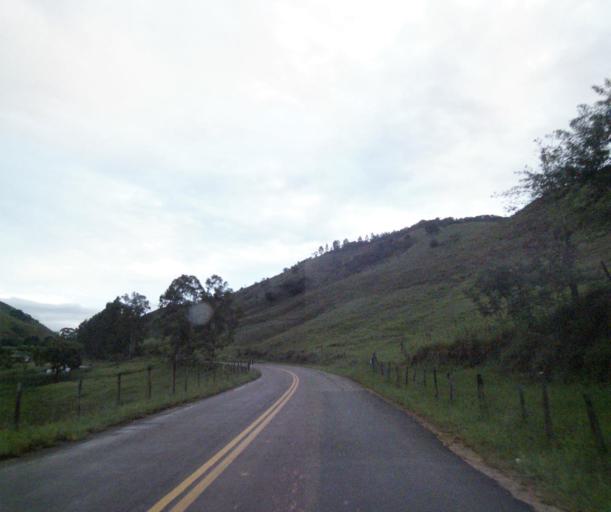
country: BR
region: Espirito Santo
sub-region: Muniz Freire
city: Muniz Freire
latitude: -20.4742
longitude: -41.4167
